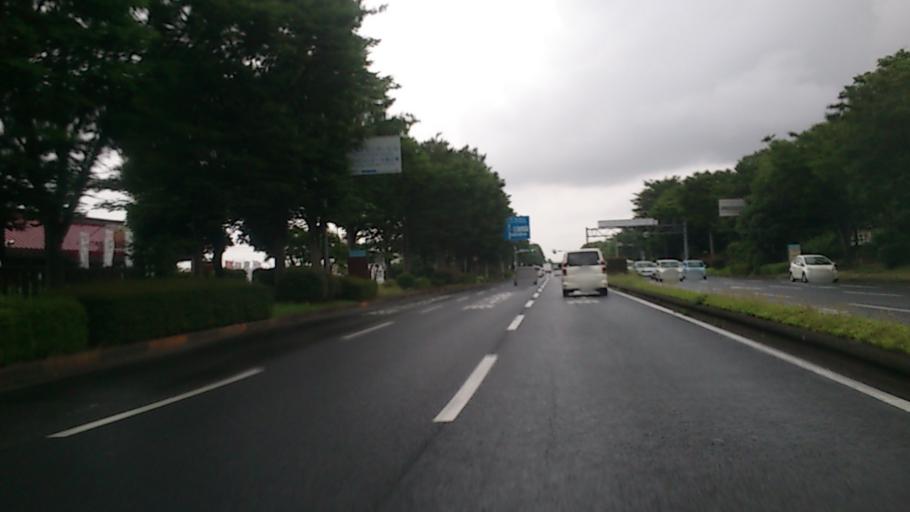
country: JP
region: Ibaraki
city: Naka
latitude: 36.0791
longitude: 140.1088
